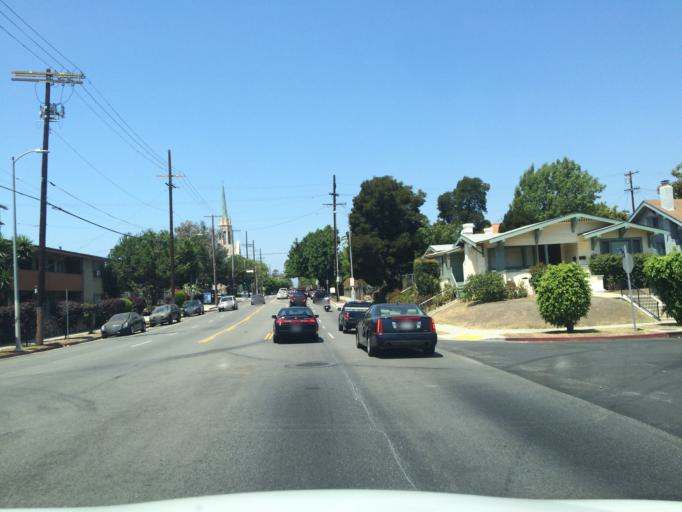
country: US
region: California
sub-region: Los Angeles County
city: Hollywood
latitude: 34.0690
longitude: -118.3126
